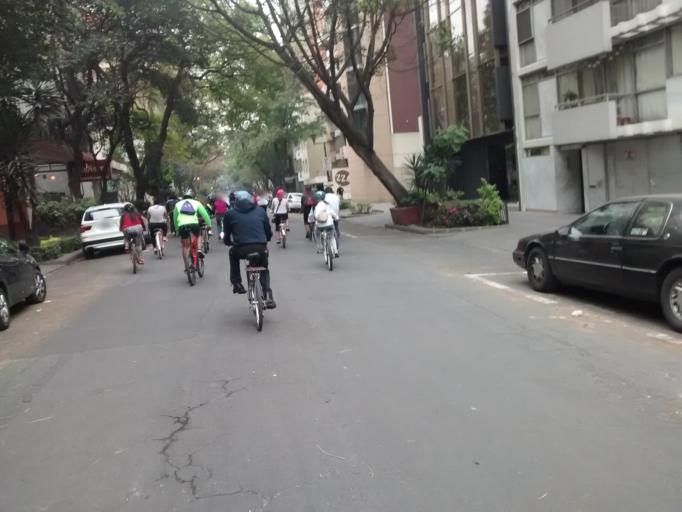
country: MX
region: Mexico City
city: Benito Juarez
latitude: 19.4232
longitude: -99.1689
